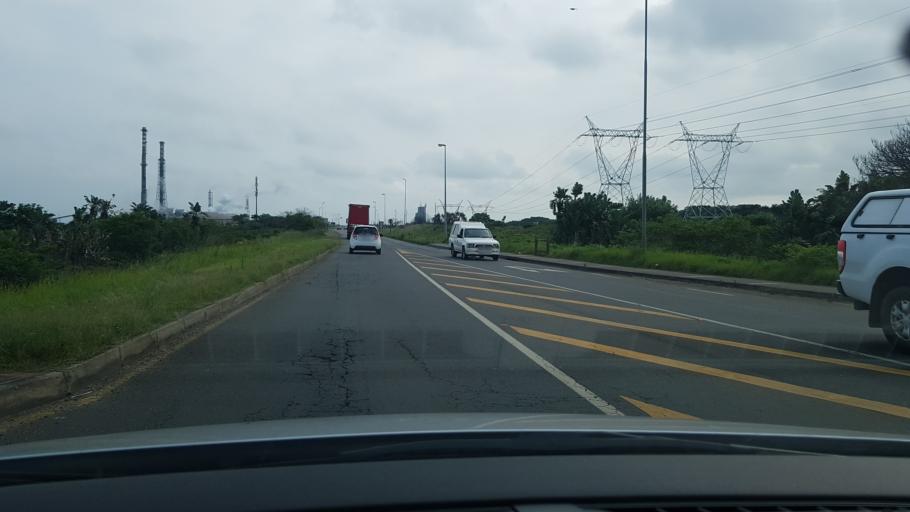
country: ZA
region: KwaZulu-Natal
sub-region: uThungulu District Municipality
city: Richards Bay
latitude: -28.7649
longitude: 32.0376
